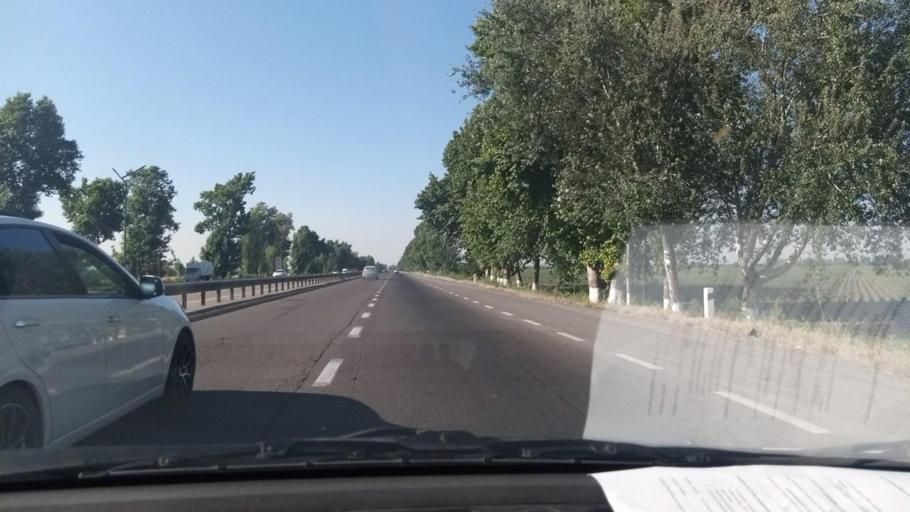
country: UZ
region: Toshkent Shahri
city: Bektemir
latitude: 41.2081
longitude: 69.4027
